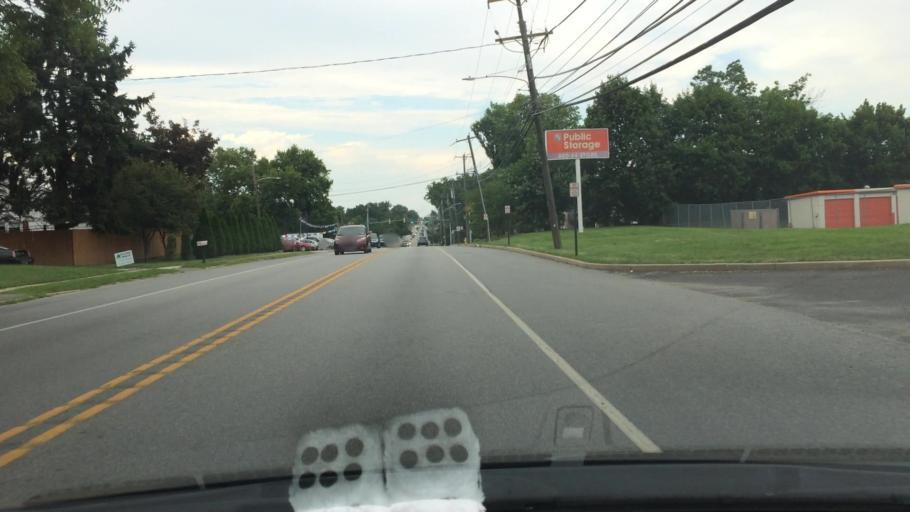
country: US
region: Pennsylvania
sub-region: Delaware County
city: Village Green-Green Ridge
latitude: 39.8494
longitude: -75.4260
